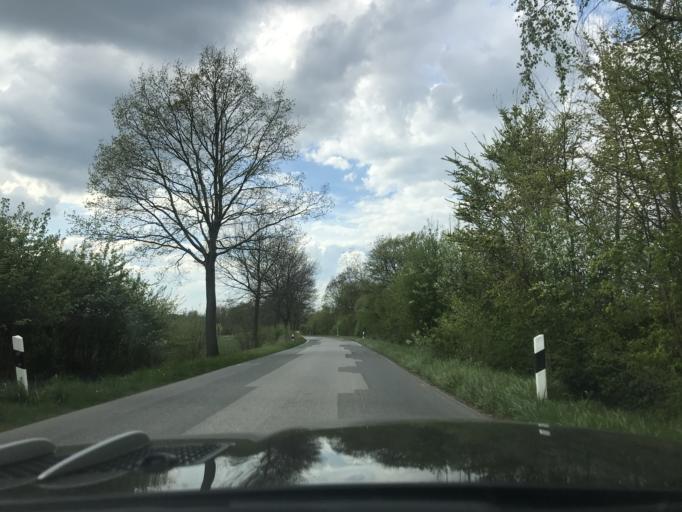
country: DE
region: Schleswig-Holstein
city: Timmendorfer Strand
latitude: 53.9588
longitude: 10.7961
